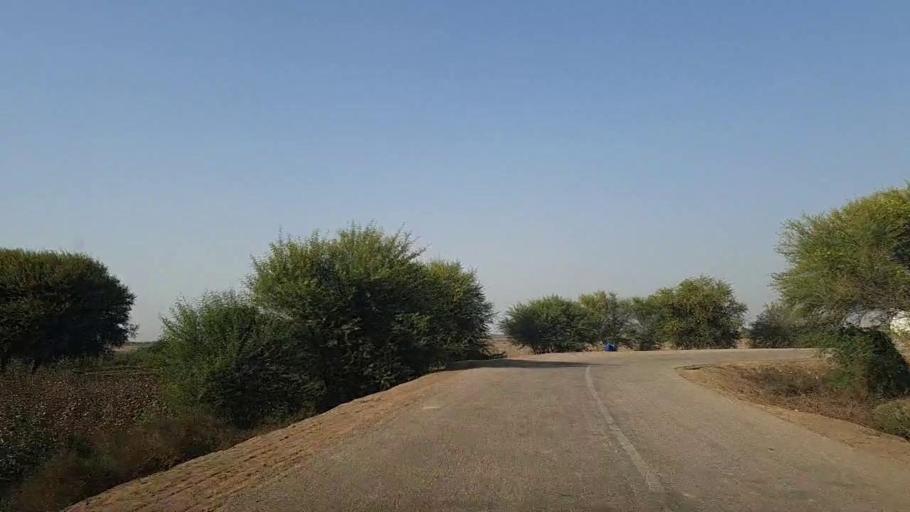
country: PK
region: Sindh
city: Mirpur Batoro
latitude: 24.5795
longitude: 68.3945
